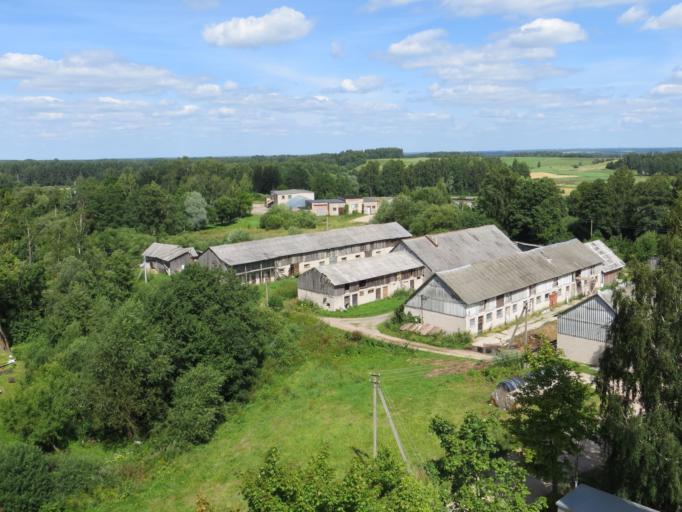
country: LT
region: Utenos apskritis
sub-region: Utena
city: Utena
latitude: 55.4883
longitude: 25.4877
